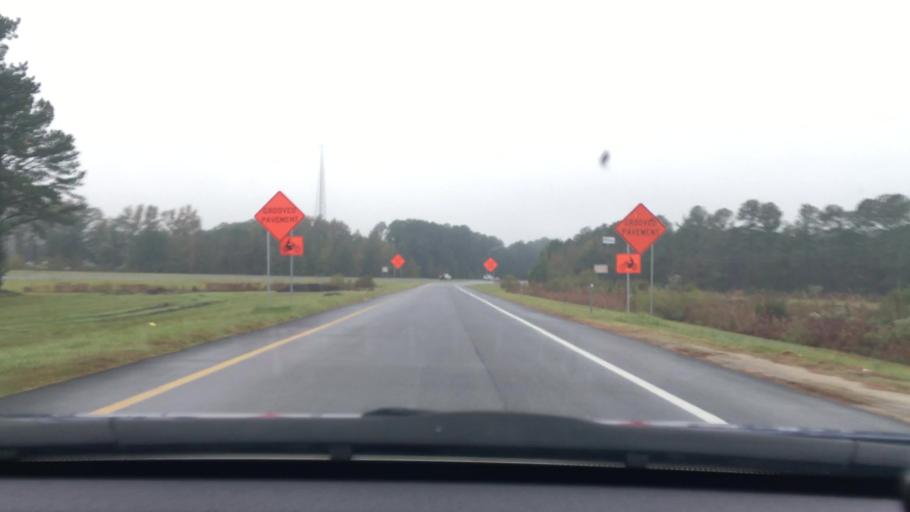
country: US
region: South Carolina
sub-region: Florence County
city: Timmonsville
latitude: 34.2073
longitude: -80.0269
